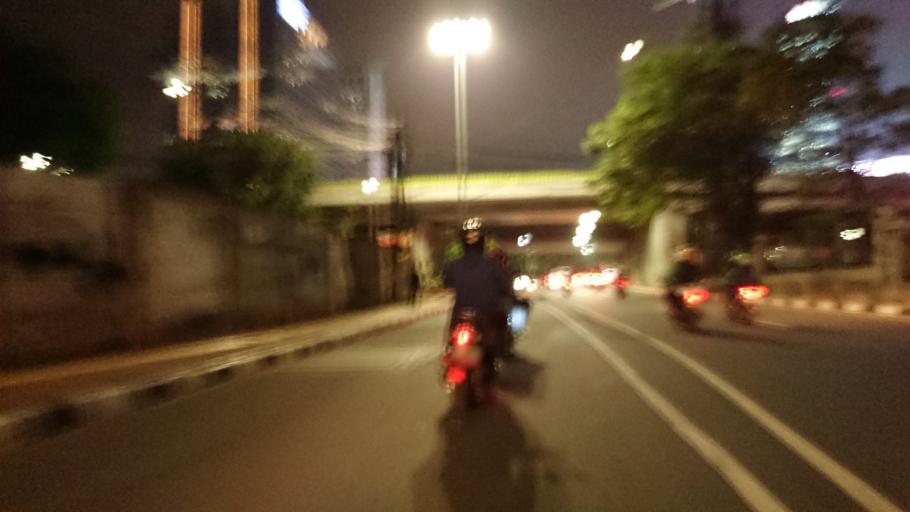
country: ID
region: Jakarta Raya
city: Jakarta
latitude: -6.2042
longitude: 106.8001
